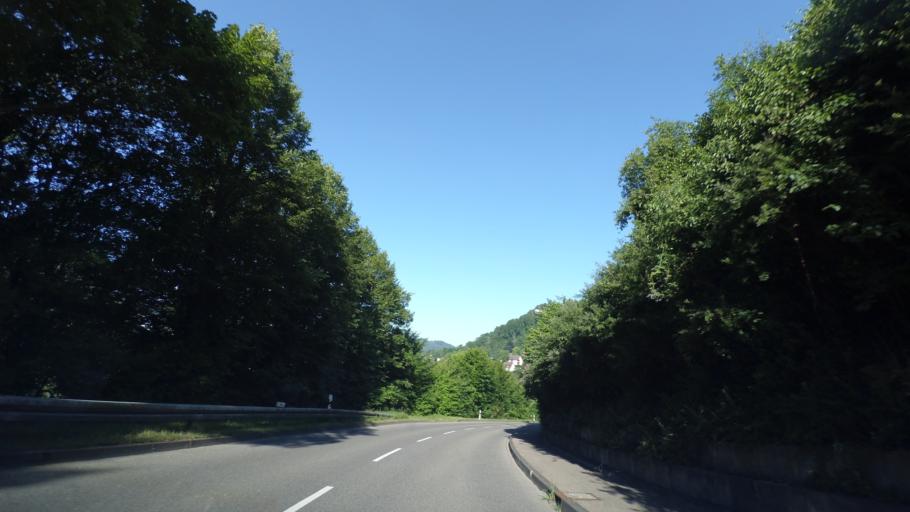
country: DE
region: Baden-Wuerttemberg
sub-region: Regierungsbezirk Stuttgart
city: Murrhardt
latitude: 48.9864
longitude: 9.5874
